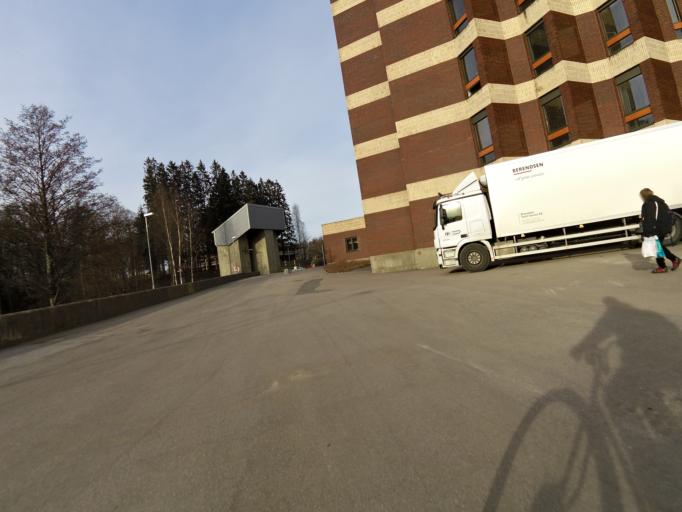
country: SE
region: Gaevleborg
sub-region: Gavle Kommun
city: Gavle
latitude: 60.6785
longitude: 17.1169
